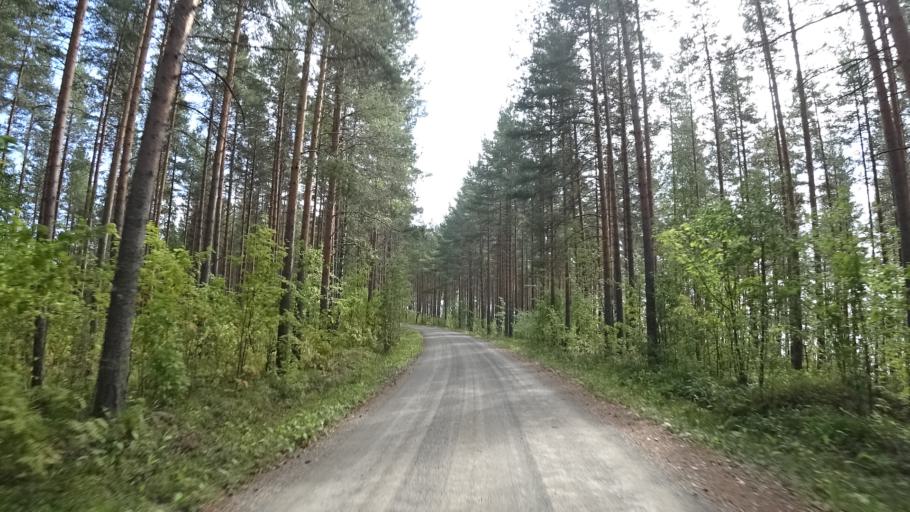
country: FI
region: North Karelia
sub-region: Keski-Karjala
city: Raeaekkylae
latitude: 62.3910
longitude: 29.7754
